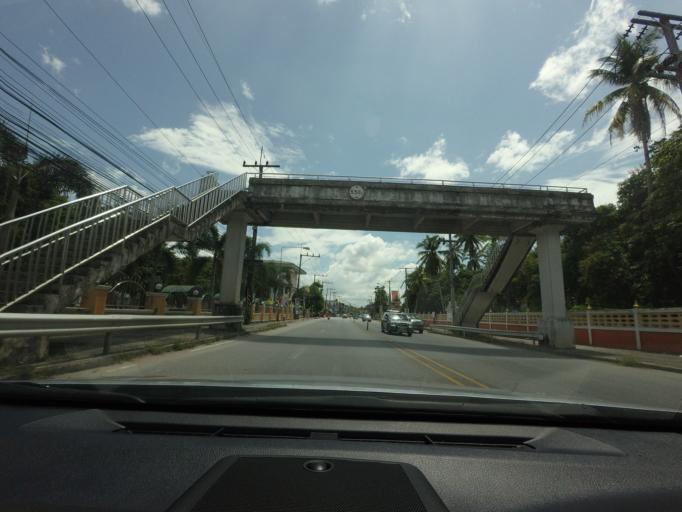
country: TH
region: Nakhon Si Thammarat
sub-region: Amphoe Nopphitam
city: Nopphitam
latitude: 8.9096
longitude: 99.8994
